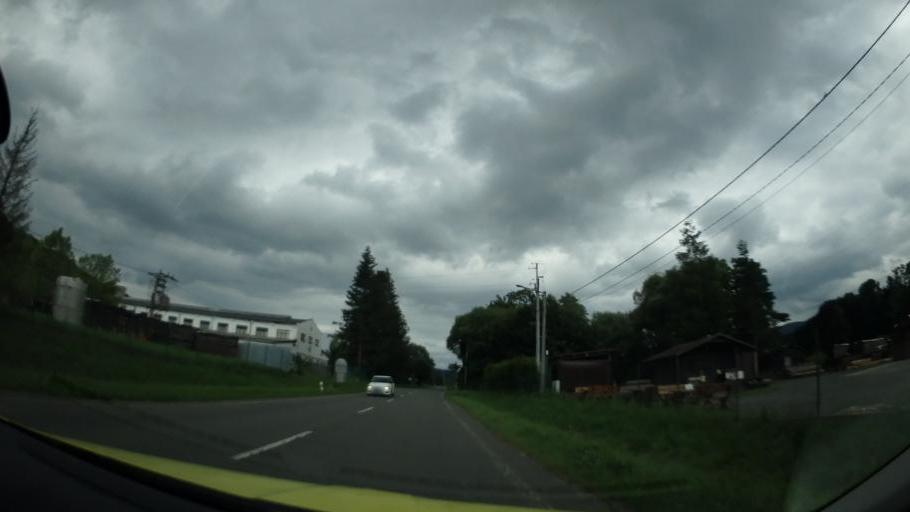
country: CZ
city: Morkov
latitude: 49.5453
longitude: 18.0655
